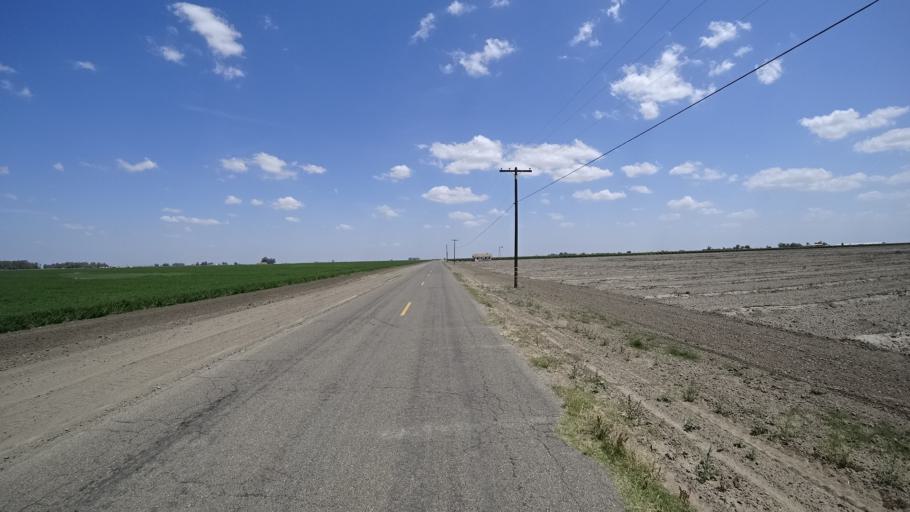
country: US
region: California
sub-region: Kings County
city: Stratford
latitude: 36.1821
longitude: -119.8102
